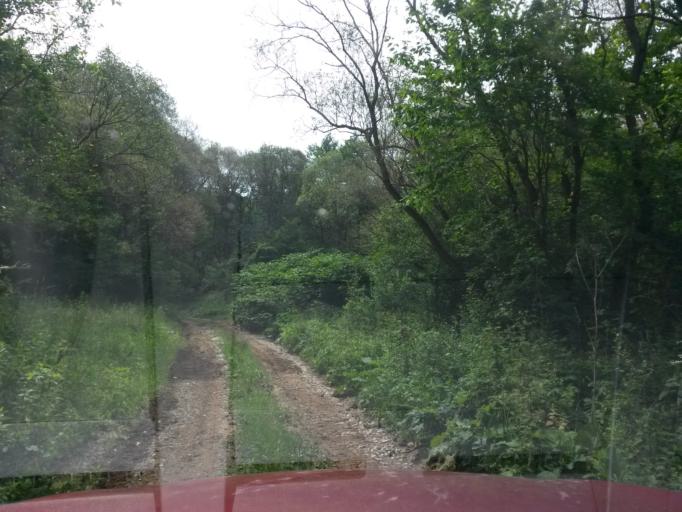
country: SK
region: Kosicky
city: Moldava nad Bodvou
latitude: 48.6658
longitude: 21.1278
